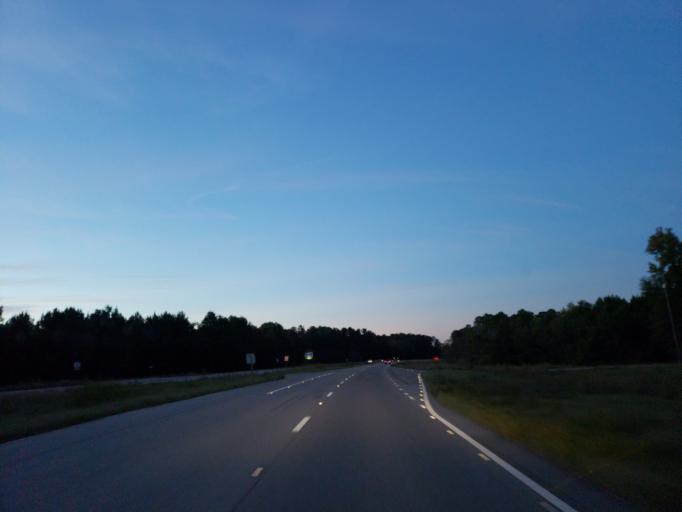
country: US
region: Mississippi
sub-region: Clarke County
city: Quitman
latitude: 31.8542
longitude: -88.7194
